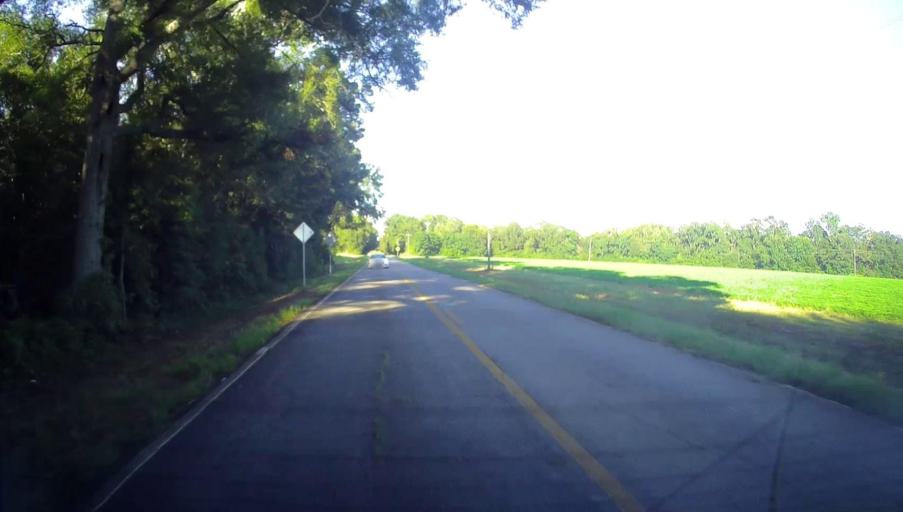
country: US
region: Georgia
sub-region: Bleckley County
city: Cochran
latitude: 32.3907
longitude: -83.4525
